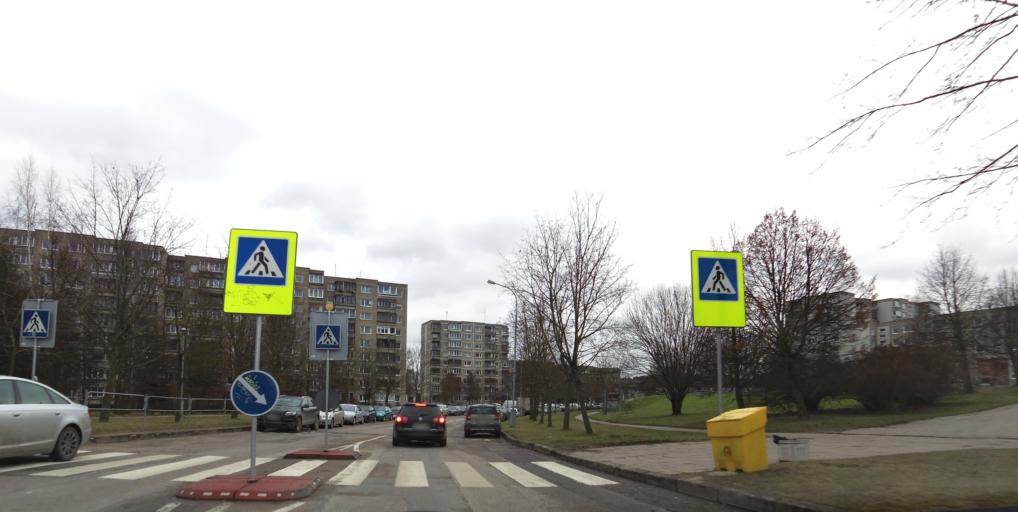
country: LT
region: Vilnius County
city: Justiniskes
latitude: 54.7208
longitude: 25.2270
